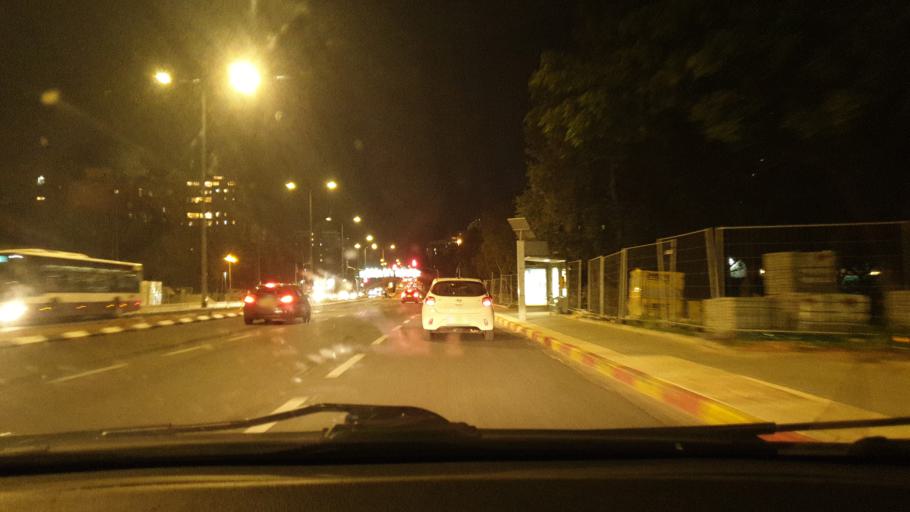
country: IL
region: Tel Aviv
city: Ramat Gan
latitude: 32.1212
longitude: 34.8038
